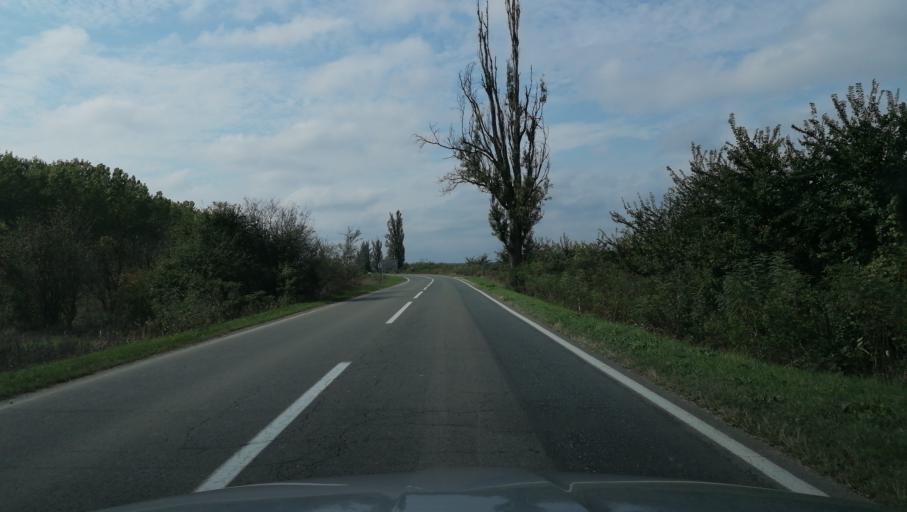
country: RS
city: Bosut
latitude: 44.9250
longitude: 19.3305
